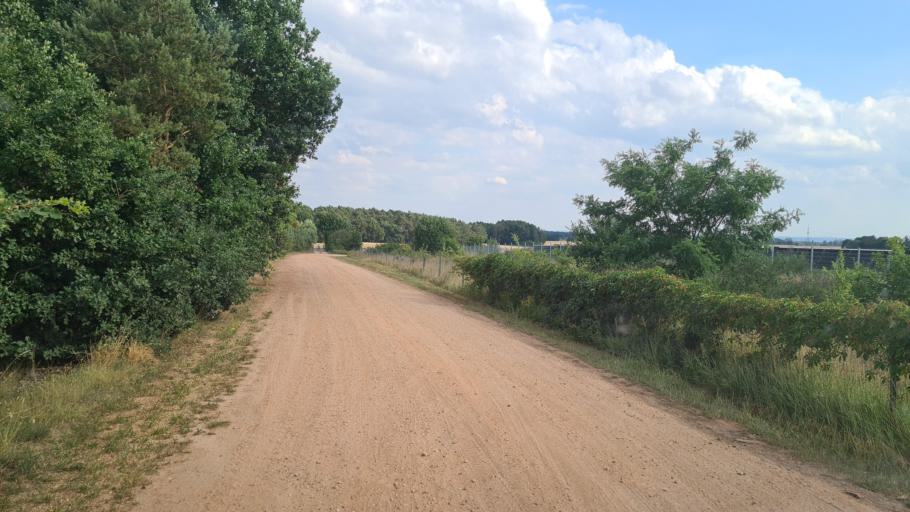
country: DE
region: Saxony-Anhalt
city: Abtsdorf
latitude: 51.9156
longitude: 12.6991
